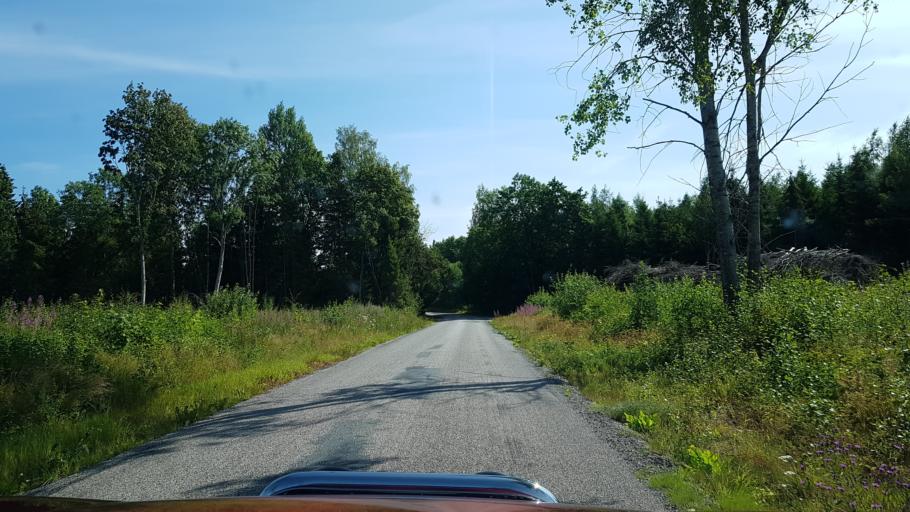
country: EE
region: Jaervamaa
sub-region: Jaerva-Jaani vald
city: Jarva-Jaani
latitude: 59.1174
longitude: 25.6821
